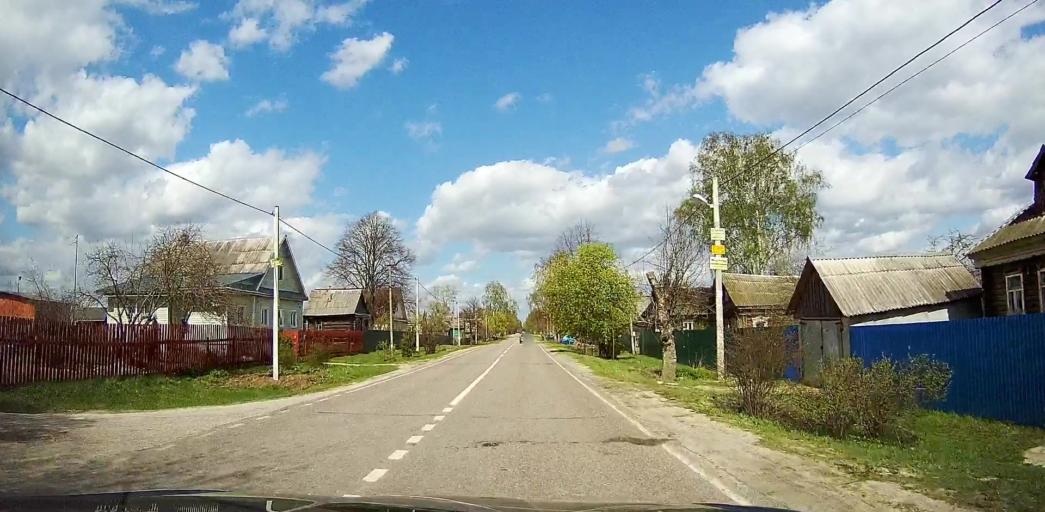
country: RU
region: Moskovskaya
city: Davydovo
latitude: 55.5757
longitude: 38.8210
